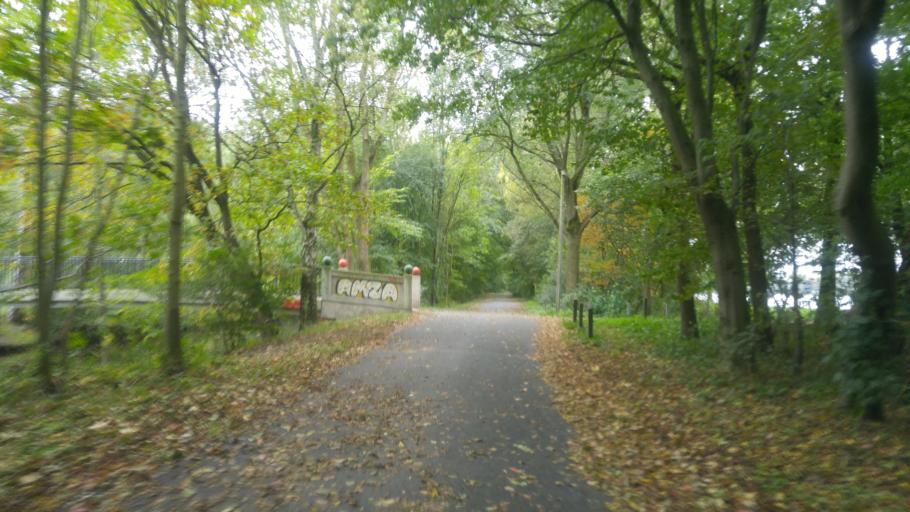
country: DE
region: Bremen
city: Bremen
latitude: 53.1083
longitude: 8.8334
